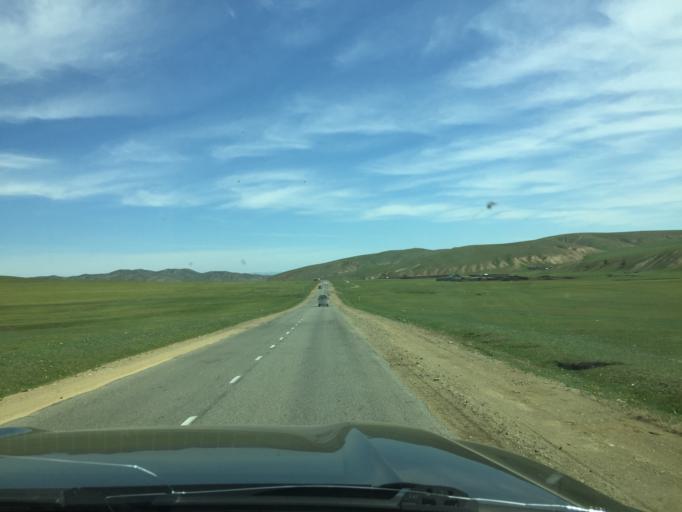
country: MN
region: Central Aimak
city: Bornuur
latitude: 48.6628
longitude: 106.1252
